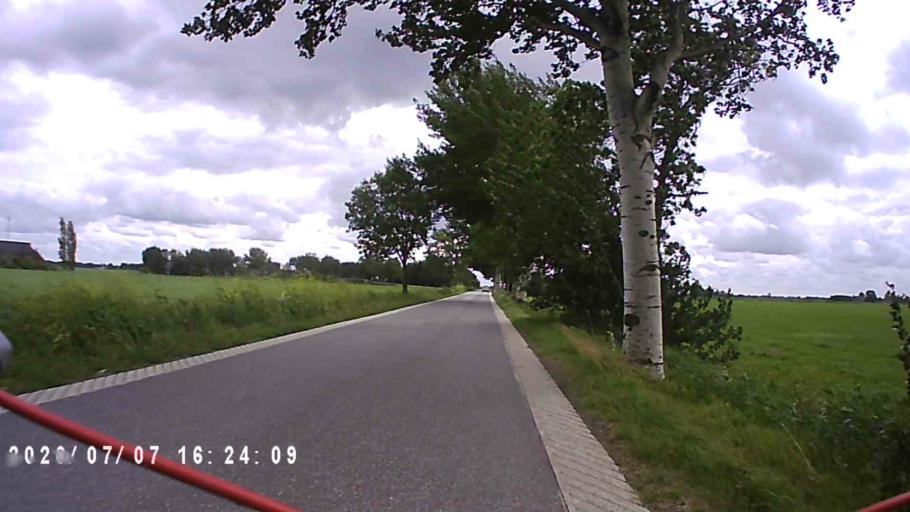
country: NL
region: Groningen
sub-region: Gemeente Winsum
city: Winsum
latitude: 53.3606
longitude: 6.5680
